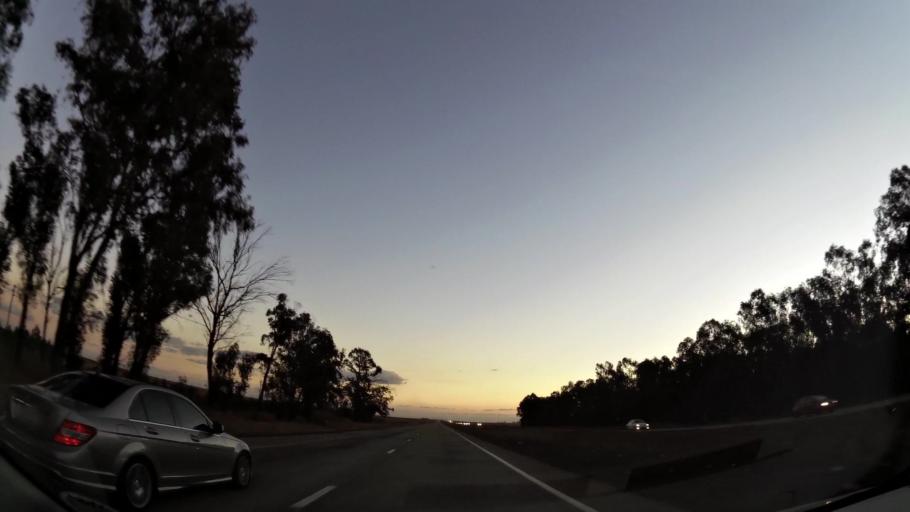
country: ZA
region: Mpumalanga
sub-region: Nkangala District Municipality
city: Witbank
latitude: -25.9767
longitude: 29.1734
